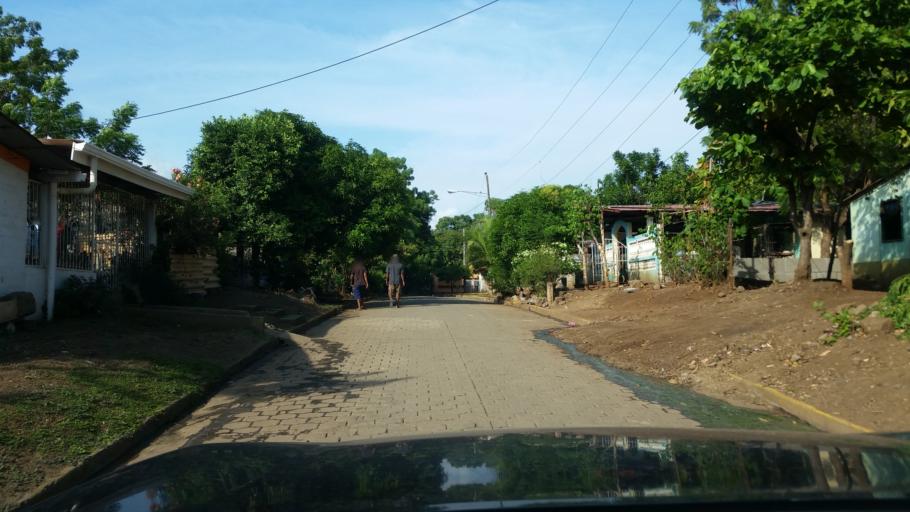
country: NI
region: Managua
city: Masachapa
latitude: 11.7888
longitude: -86.5153
